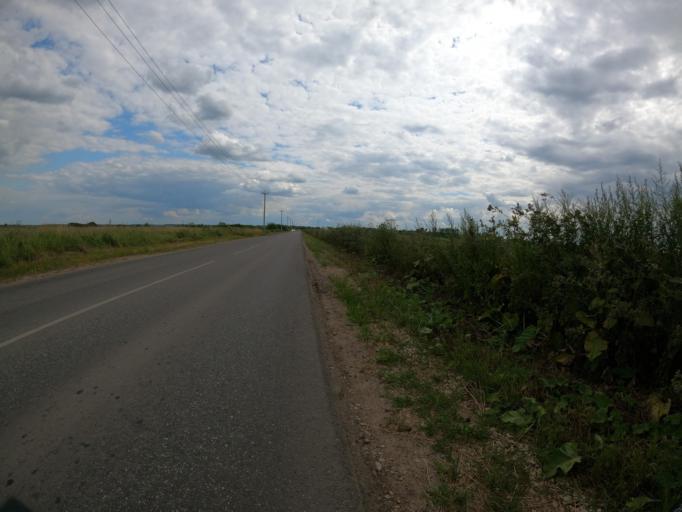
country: RU
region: Moskovskaya
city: Ramenskoye
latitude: 55.5012
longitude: 38.2320
